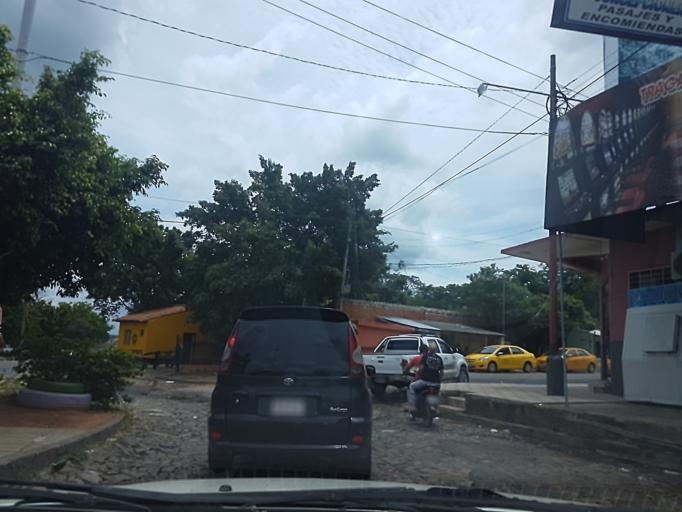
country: PY
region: Central
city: Colonia Mariano Roque Alonso
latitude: -25.1881
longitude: -57.5420
